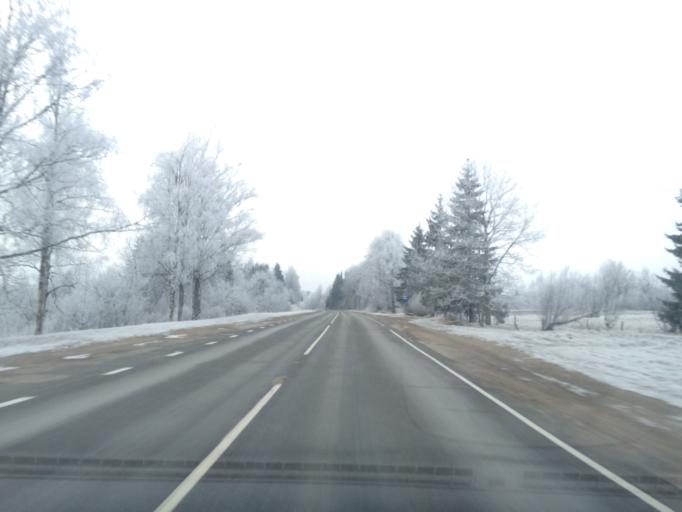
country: LV
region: Rezekne
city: Rezekne
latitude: 56.6305
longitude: 27.4656
